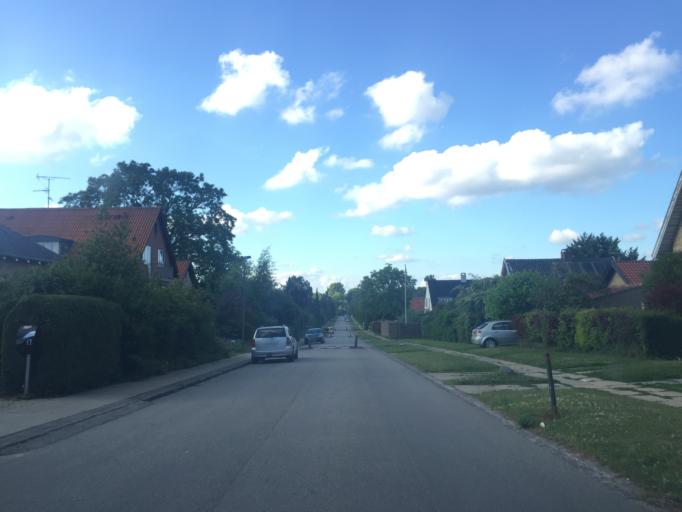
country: DK
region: Capital Region
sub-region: Kobenhavn
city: Vanlose
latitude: 55.7065
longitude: 12.4984
